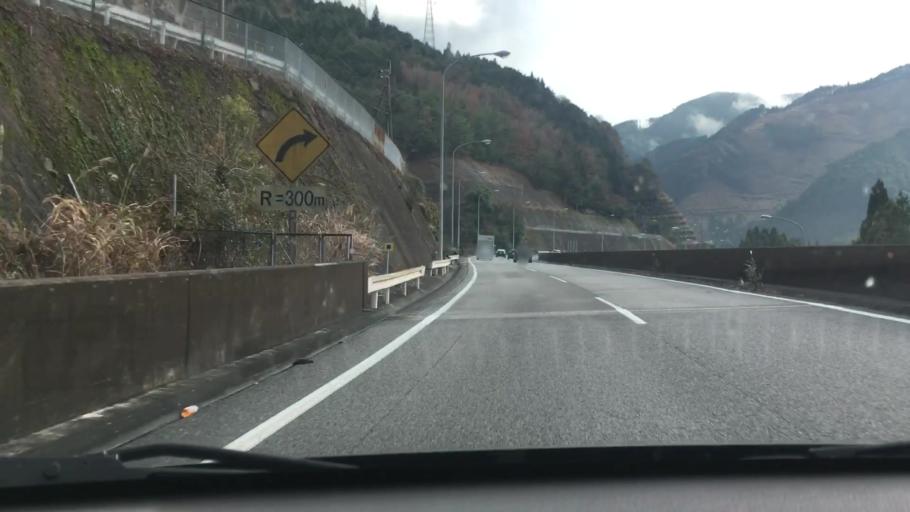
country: JP
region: Kumamoto
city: Yatsushiro
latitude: 32.4073
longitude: 130.6972
